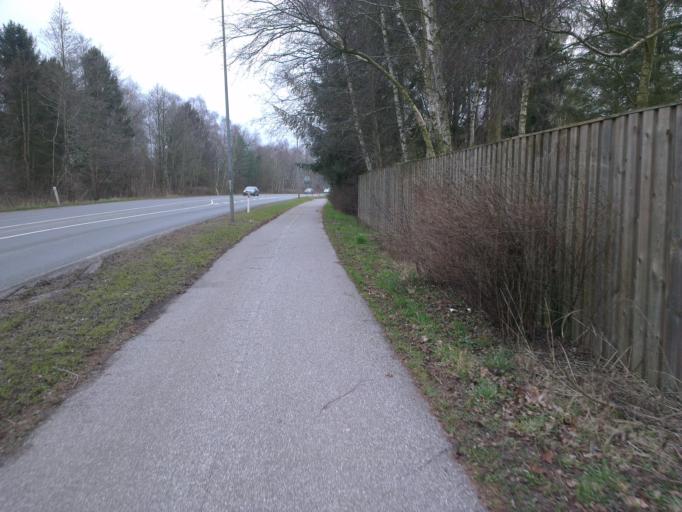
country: DK
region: Capital Region
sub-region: Frederikssund Kommune
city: Frederikssund
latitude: 55.8552
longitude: 12.0706
